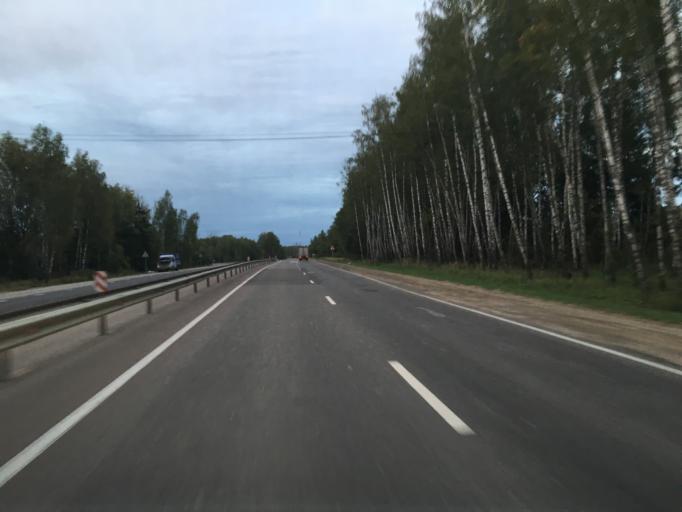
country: RU
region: Kaluga
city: Kaluga
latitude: 54.6343
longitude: 36.2962
